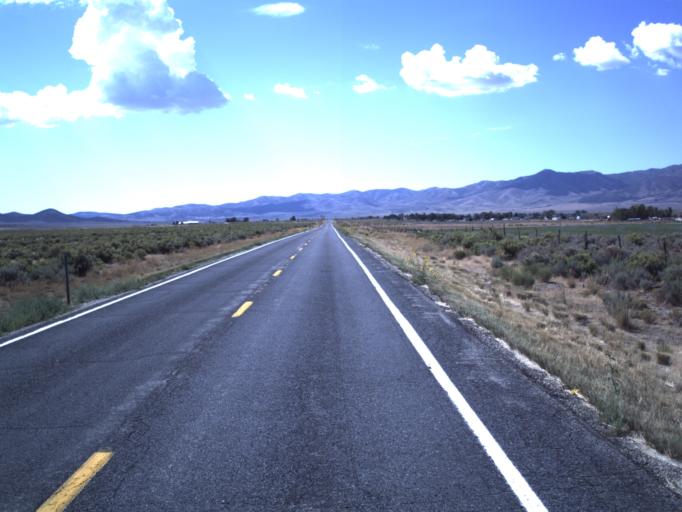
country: US
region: Utah
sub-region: Tooele County
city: Tooele
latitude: 40.1157
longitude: -112.4308
